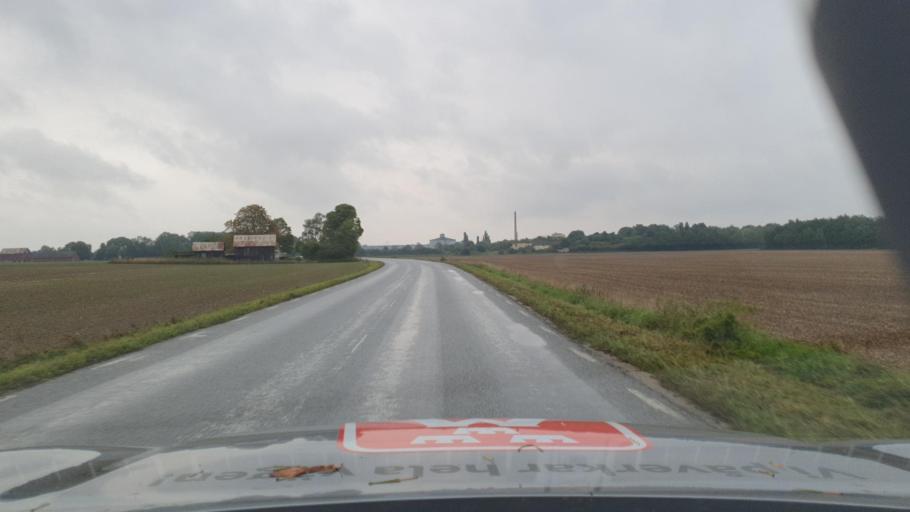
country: SE
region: Gotland
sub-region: Gotland
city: Visby
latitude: 57.5030
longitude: 18.4340
